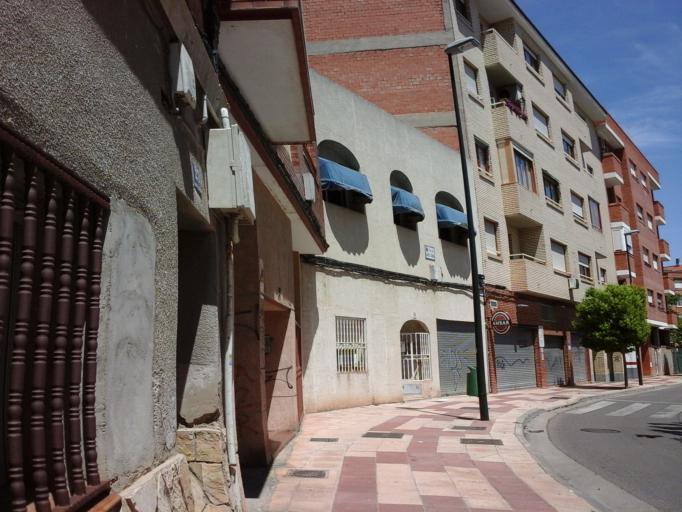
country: ES
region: Aragon
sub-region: Provincia de Zaragoza
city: Zaragoza
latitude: 41.6314
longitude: -0.8795
